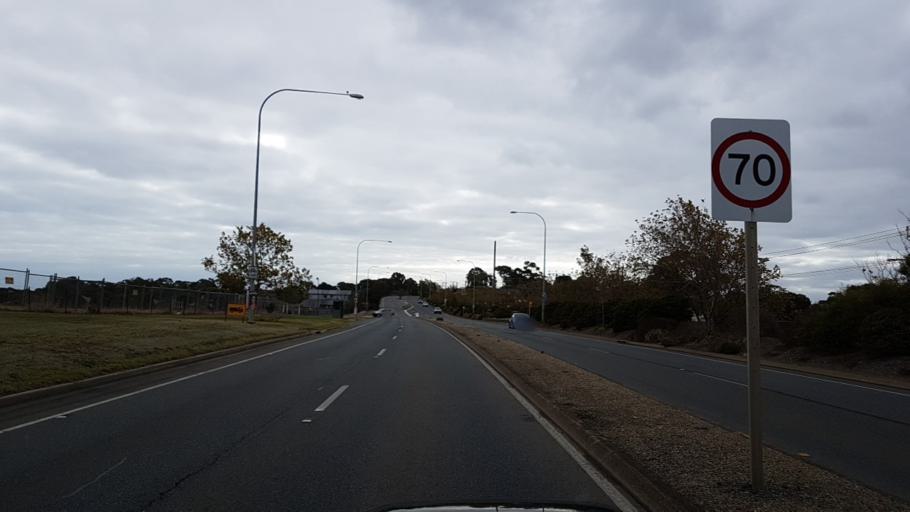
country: AU
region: South Australia
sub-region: Onkaparinga
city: Bedford Park
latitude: -35.0494
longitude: 138.5726
